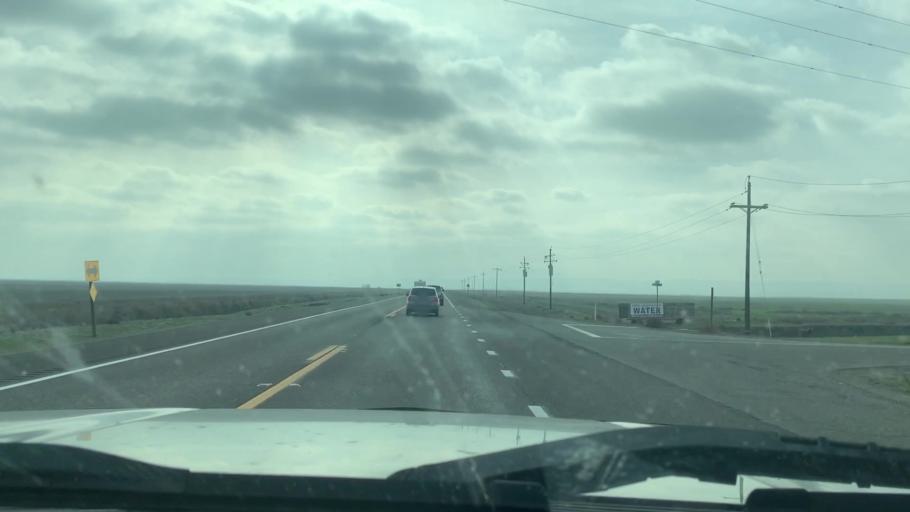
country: US
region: California
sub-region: Kings County
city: Kettleman City
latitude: 36.0942
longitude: -119.9105
